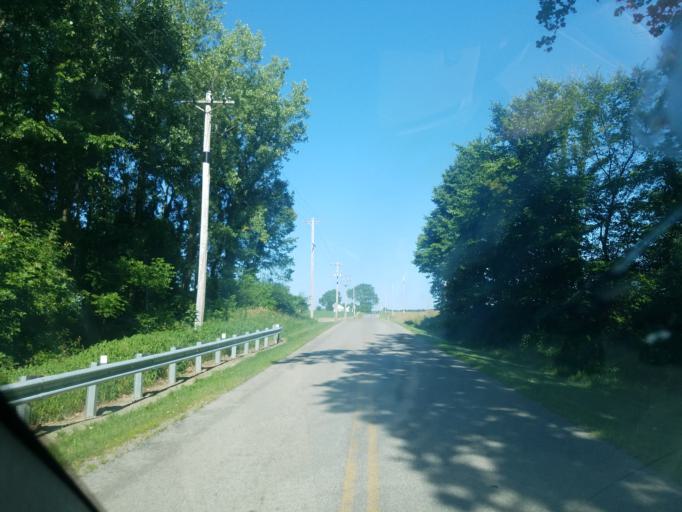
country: US
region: Ohio
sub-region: Logan County
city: Northwood
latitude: 40.4407
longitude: -83.6791
